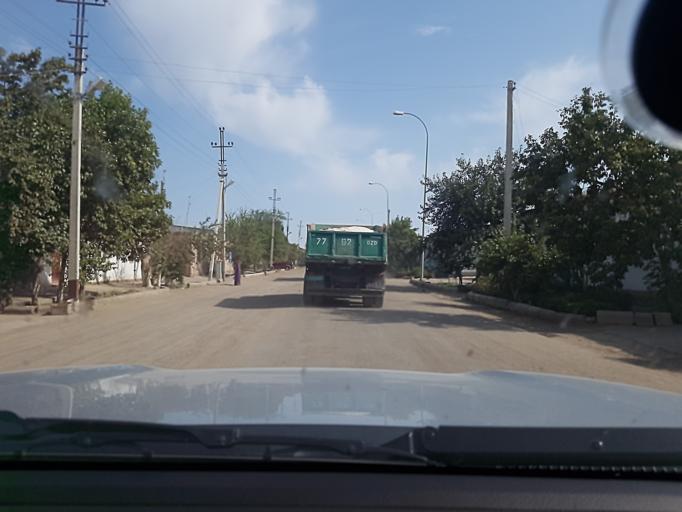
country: TM
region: Dasoguz
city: Dasoguz
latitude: 41.8274
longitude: 59.9790
